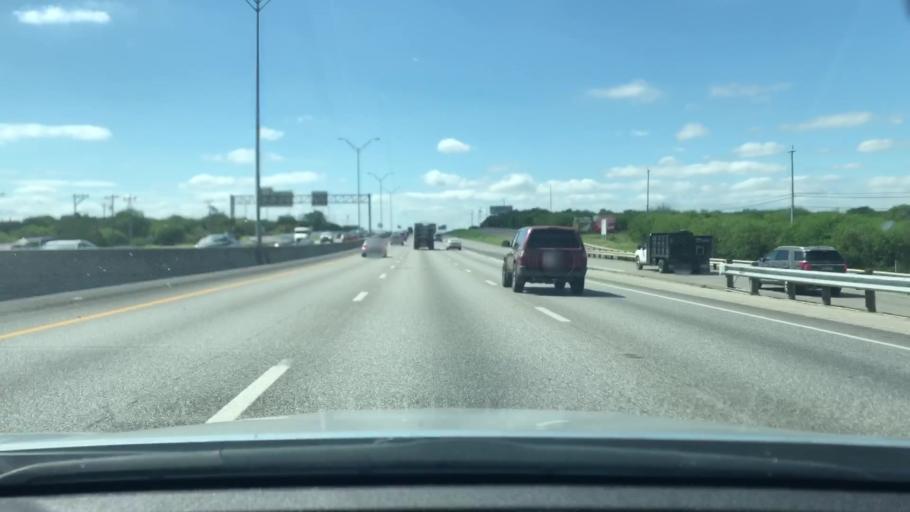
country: US
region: Texas
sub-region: Guadalupe County
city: Northcliff
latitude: 29.6245
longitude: -98.2429
